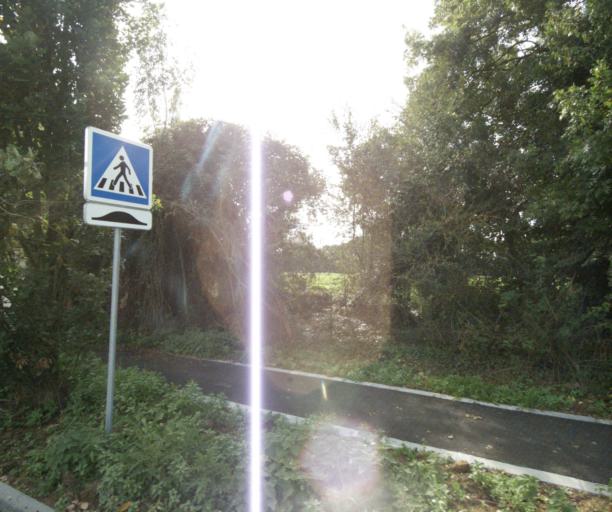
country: FR
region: Nord-Pas-de-Calais
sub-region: Departement du Nord
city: Radinghem-en-Weppes
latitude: 50.5986
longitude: 2.9226
